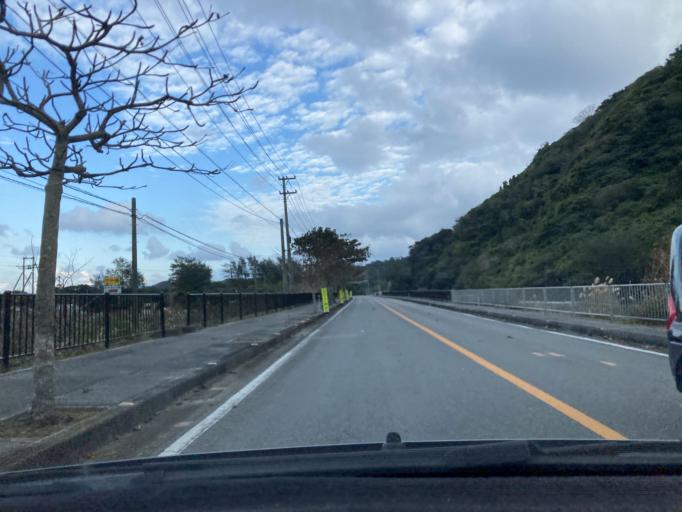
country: JP
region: Okinawa
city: Nago
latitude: 26.8396
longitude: 128.2896
